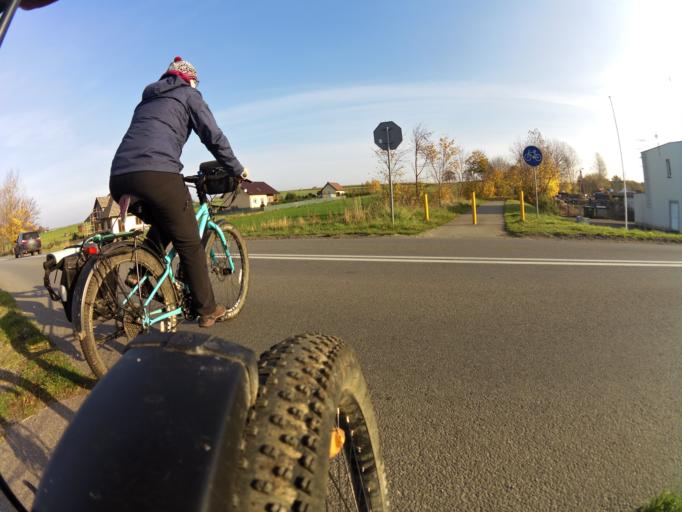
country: PL
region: Pomeranian Voivodeship
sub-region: Powiat pucki
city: Krokowa
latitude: 54.7835
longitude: 18.1700
